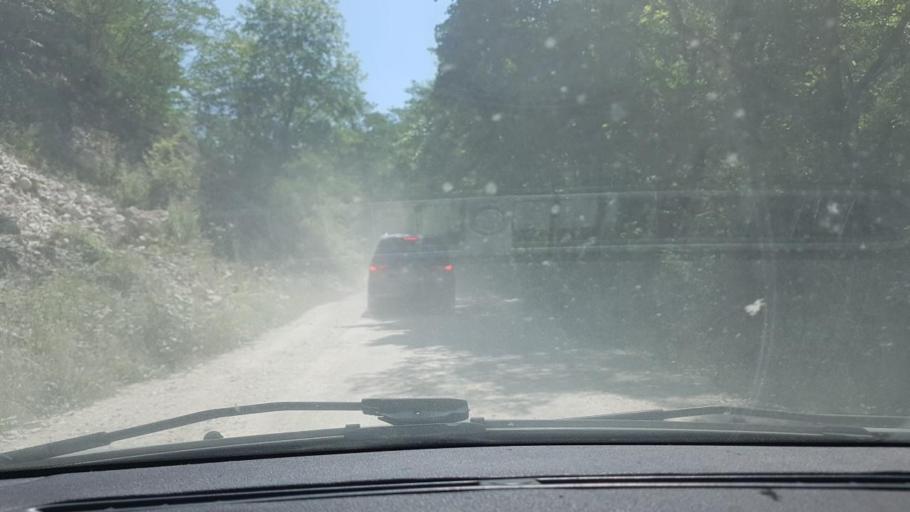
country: BA
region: Federation of Bosnia and Herzegovina
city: Orasac
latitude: 44.6493
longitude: 16.0322
